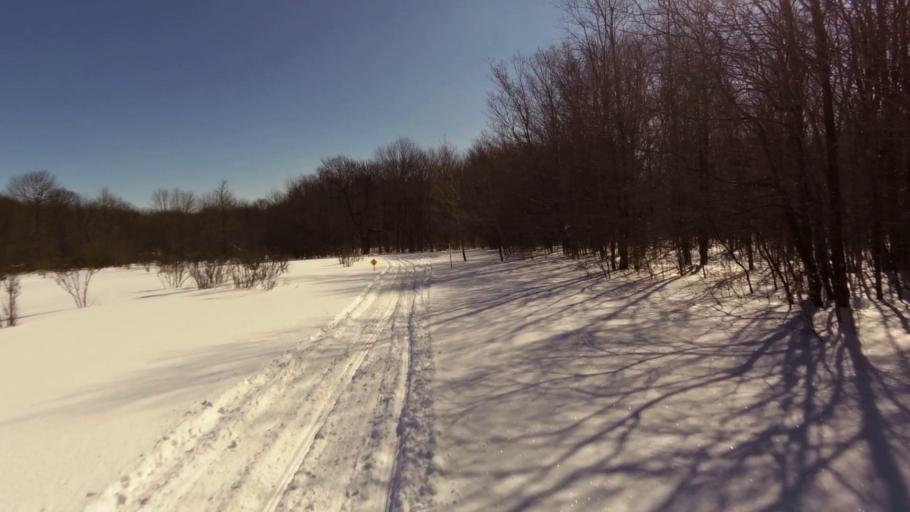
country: US
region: New York
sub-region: Cattaraugus County
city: Franklinville
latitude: 42.3464
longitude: -78.3803
